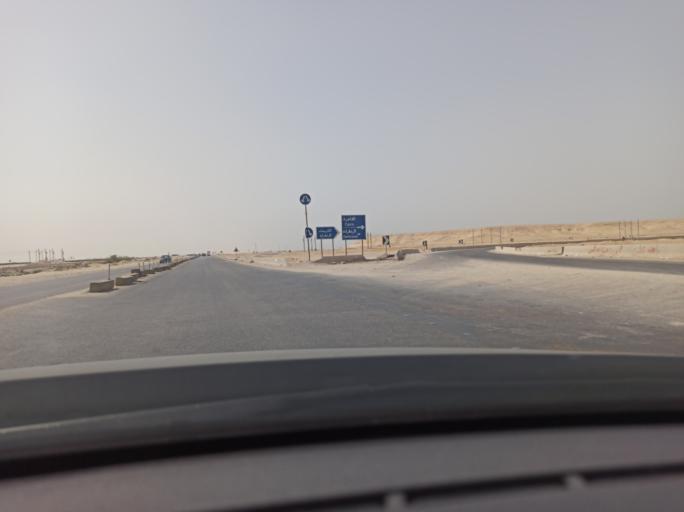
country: EG
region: Muhafazat al Fayyum
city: Al Wasitah
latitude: 29.2871
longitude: 31.2716
